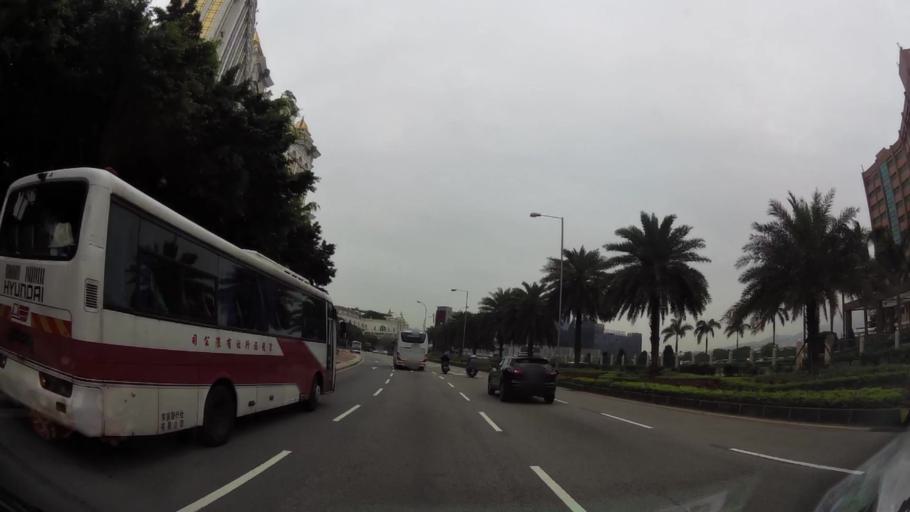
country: MO
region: Macau
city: Macau
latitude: 22.1500
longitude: 113.5513
